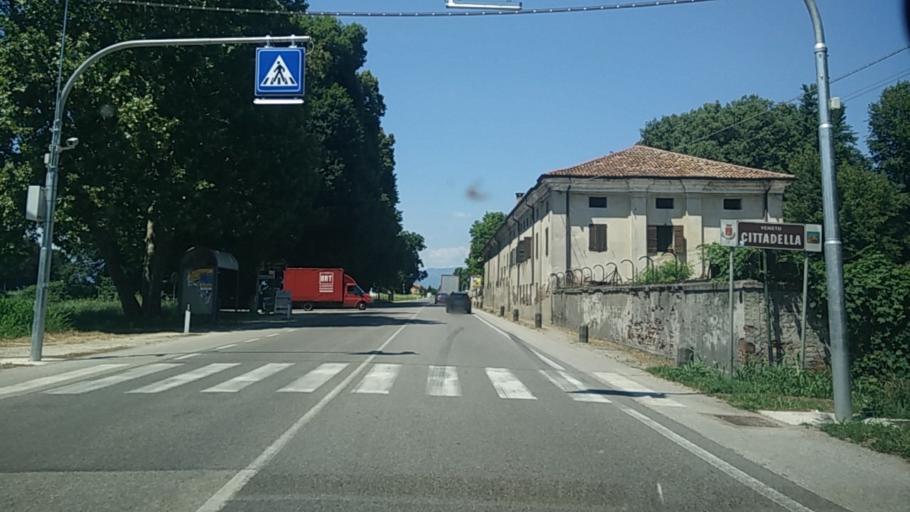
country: IT
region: Veneto
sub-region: Provincia di Padova
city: San Giorgio in Bosco
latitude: 45.6065
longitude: 11.8001
